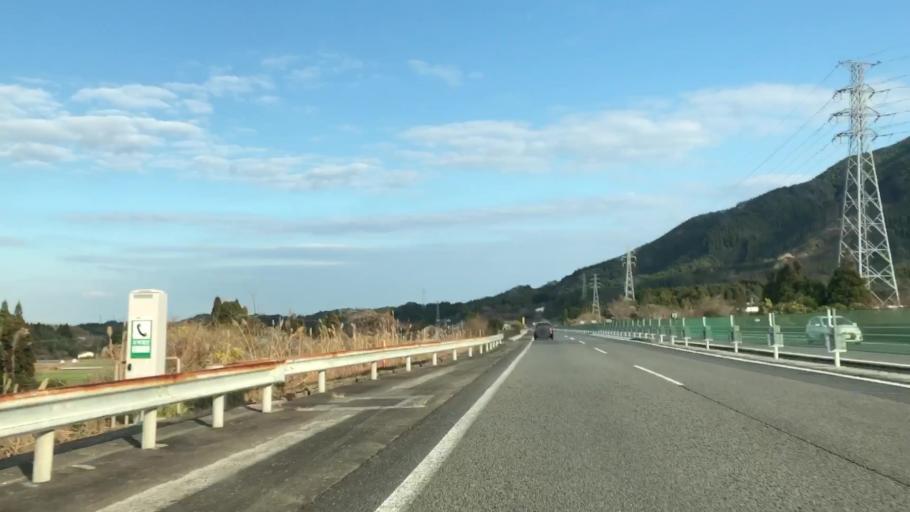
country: JP
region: Miyazaki
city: Miyazaki-shi
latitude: 31.8328
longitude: 131.3295
